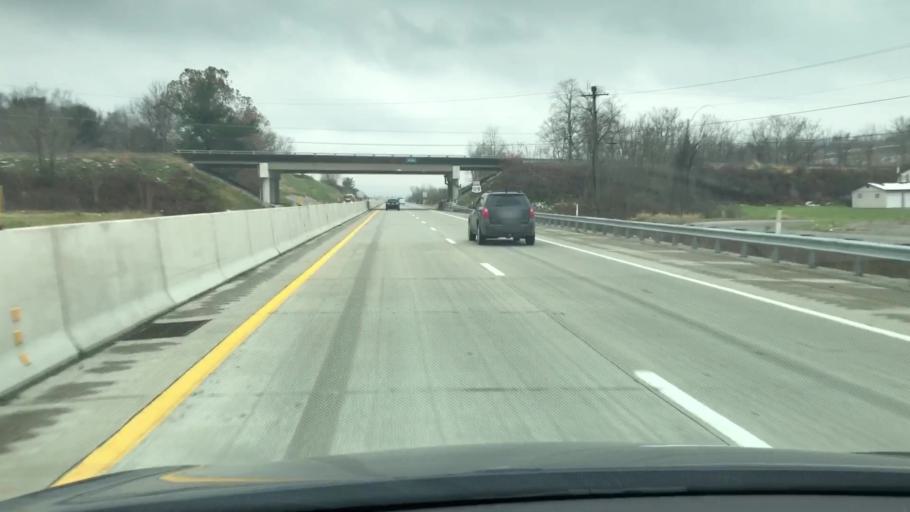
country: US
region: Pennsylvania
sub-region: Westmoreland County
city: Mount Pleasant
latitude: 40.1498
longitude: -79.5608
